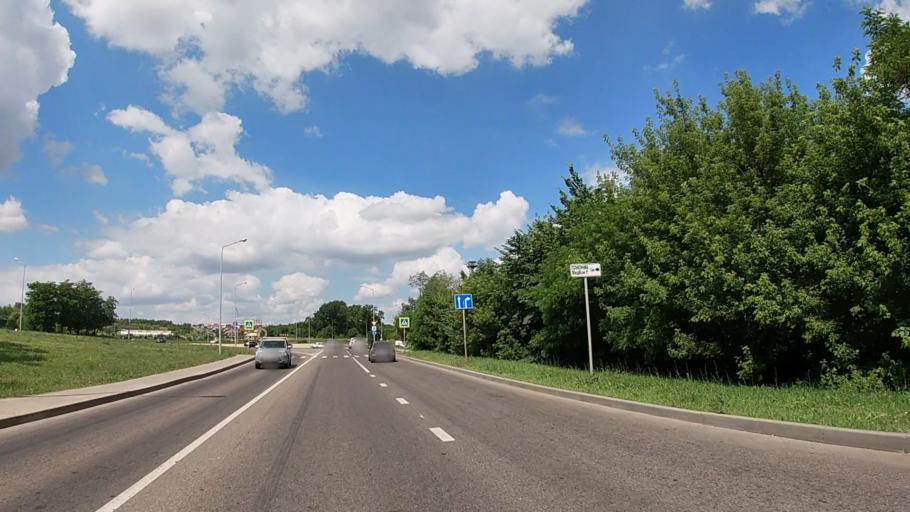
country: RU
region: Belgorod
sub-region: Belgorodskiy Rayon
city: Belgorod
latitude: 50.5949
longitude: 36.5539
